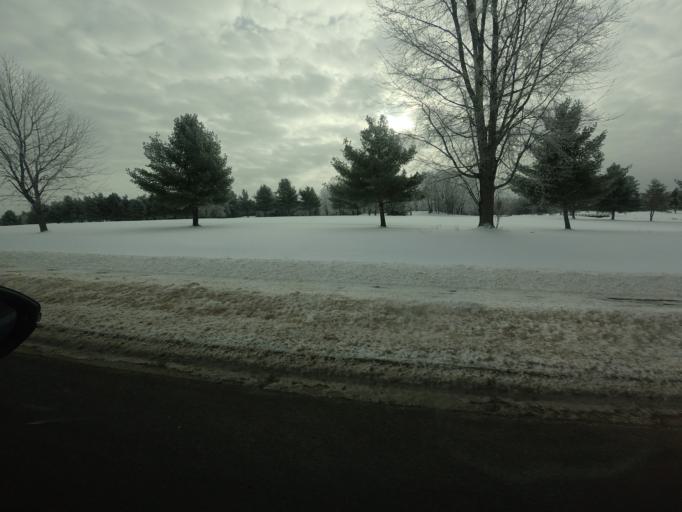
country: CA
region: New Brunswick
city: Oromocto
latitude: 45.8465
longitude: -66.5013
